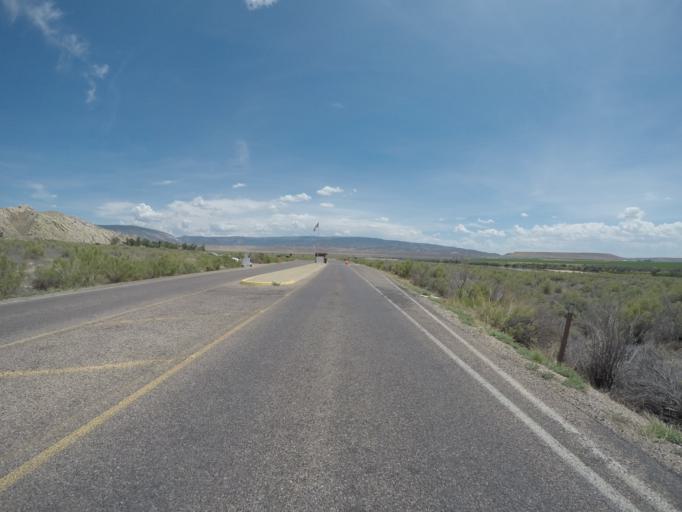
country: US
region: Utah
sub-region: Uintah County
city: Naples
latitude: 40.4371
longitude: -109.3098
